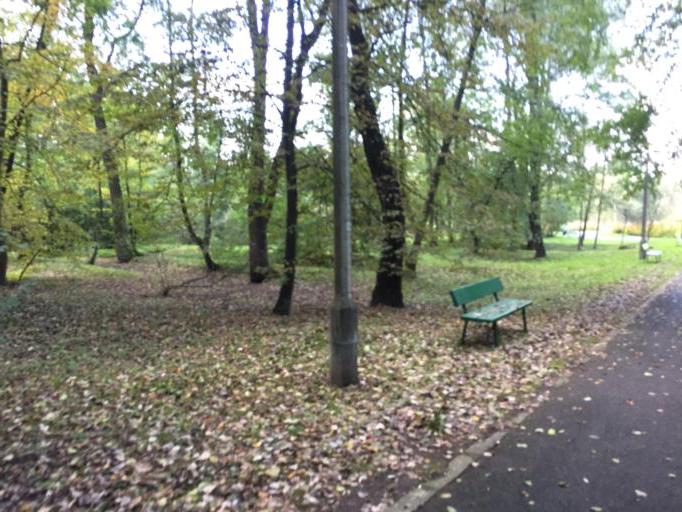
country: PL
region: Lesser Poland Voivodeship
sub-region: Powiat wielicki
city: Czarnochowice
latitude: 50.0199
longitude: 20.0025
